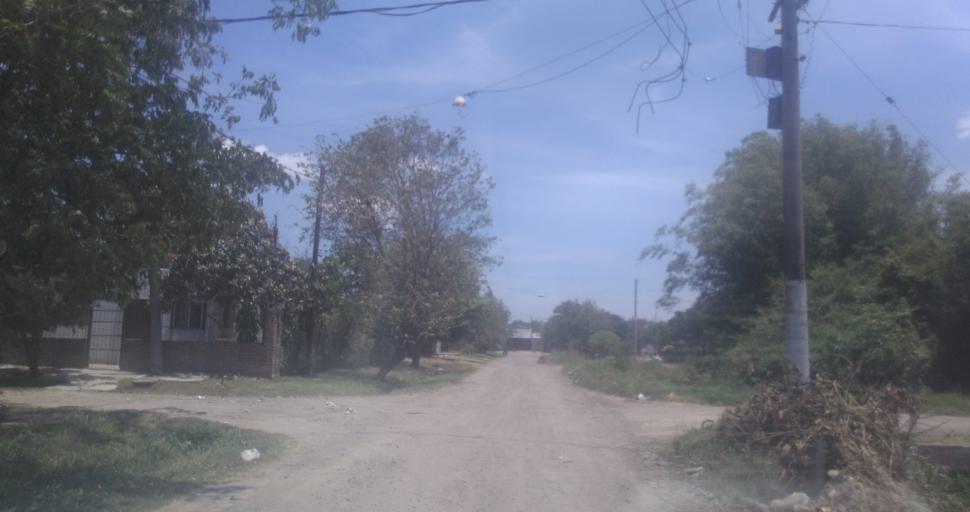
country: AR
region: Chaco
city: Fontana
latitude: -27.4209
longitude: -59.0373
